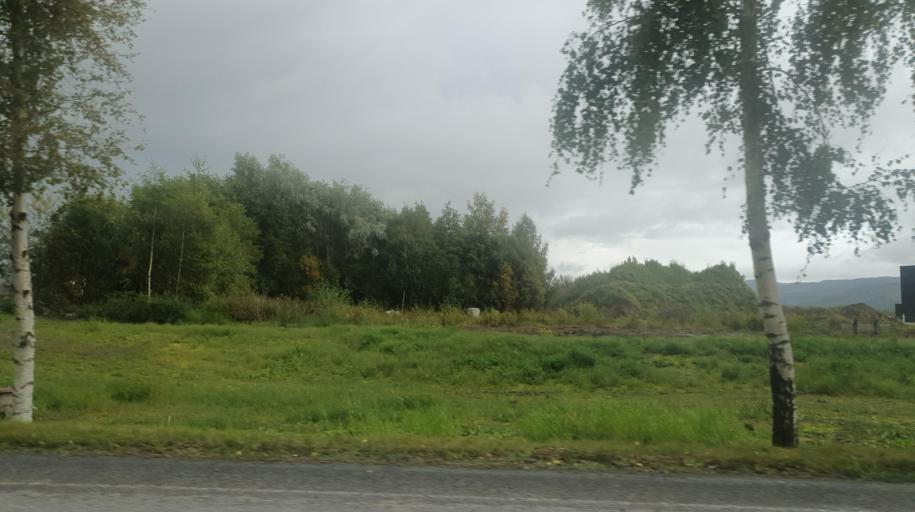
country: NO
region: Nord-Trondelag
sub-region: Verdal
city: Verdal
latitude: 63.7905
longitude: 11.4885
